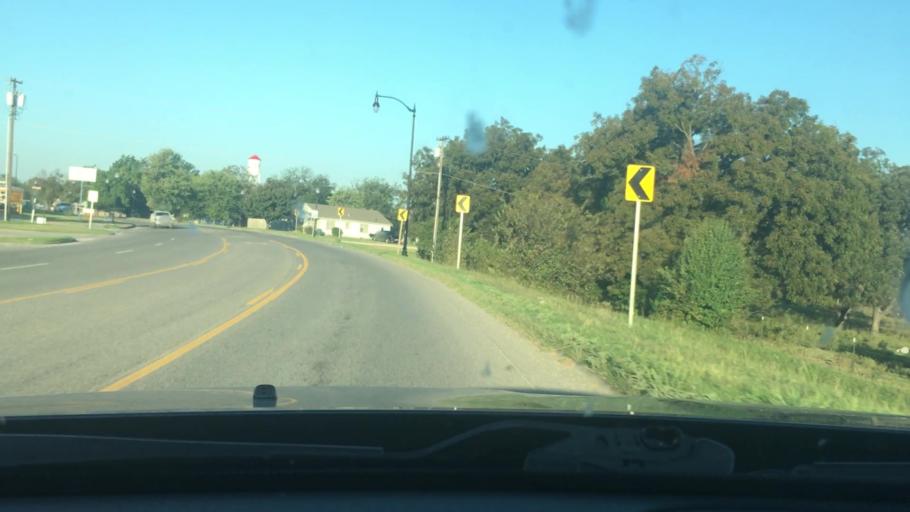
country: US
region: Oklahoma
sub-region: Murray County
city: Davis
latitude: 34.5072
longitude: -97.1102
